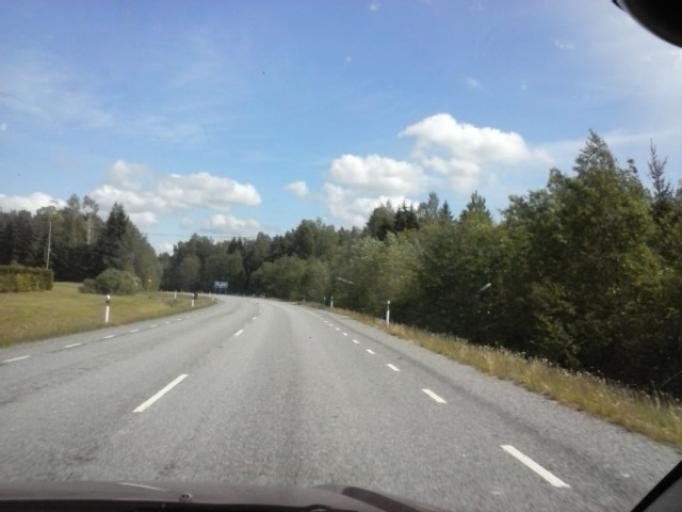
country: EE
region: Raplamaa
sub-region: Rapla vald
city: Rapla
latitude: 58.9909
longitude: 24.7771
